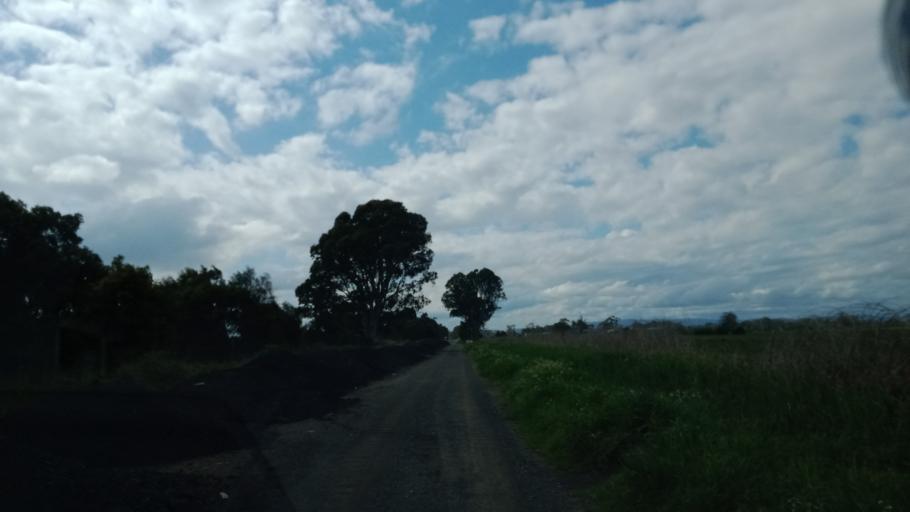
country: AU
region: Victoria
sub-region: Frankston
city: Sandhurst
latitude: -38.0847
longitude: 145.2196
